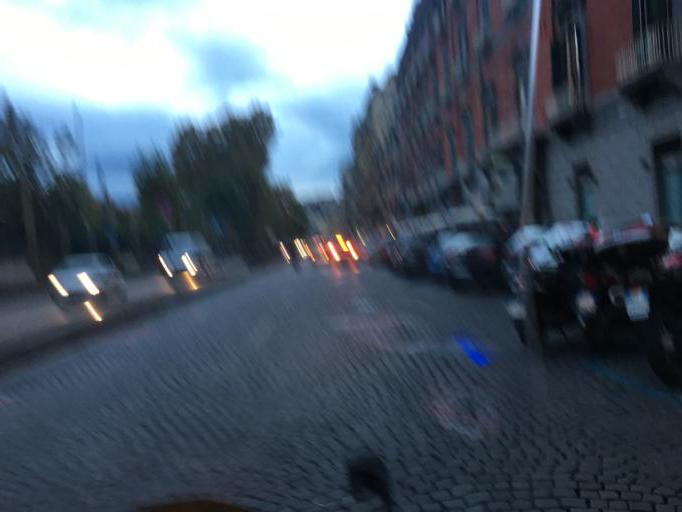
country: IT
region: Campania
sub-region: Provincia di Napoli
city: Napoli
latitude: 40.8332
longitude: 14.2395
